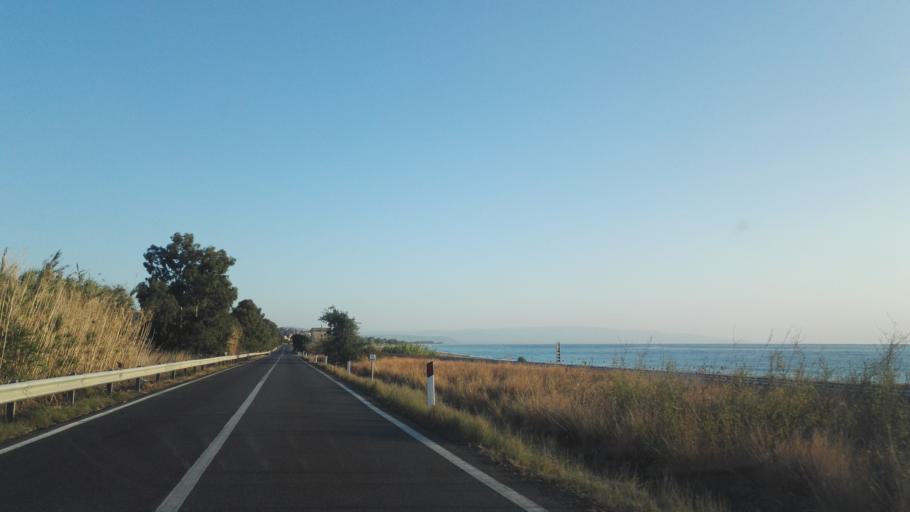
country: IT
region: Calabria
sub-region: Provincia di Catanzaro
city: Santa Caterina dello Ionio Marina
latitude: 38.5058
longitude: 16.5758
